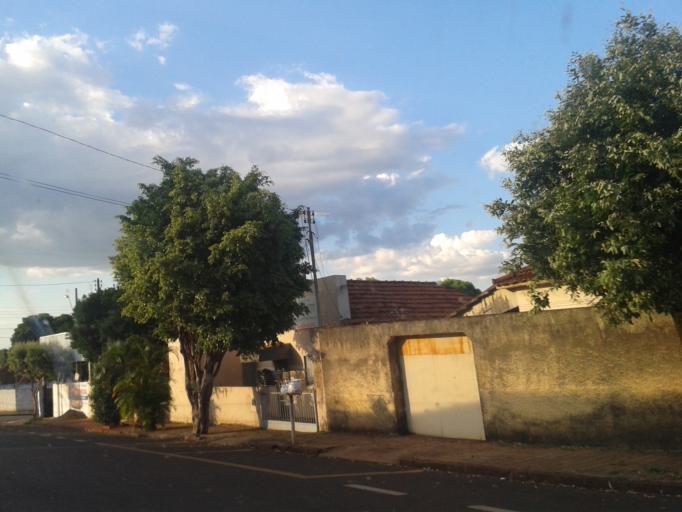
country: BR
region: Minas Gerais
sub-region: Ituiutaba
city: Ituiutaba
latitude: -18.9706
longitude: -49.4601
